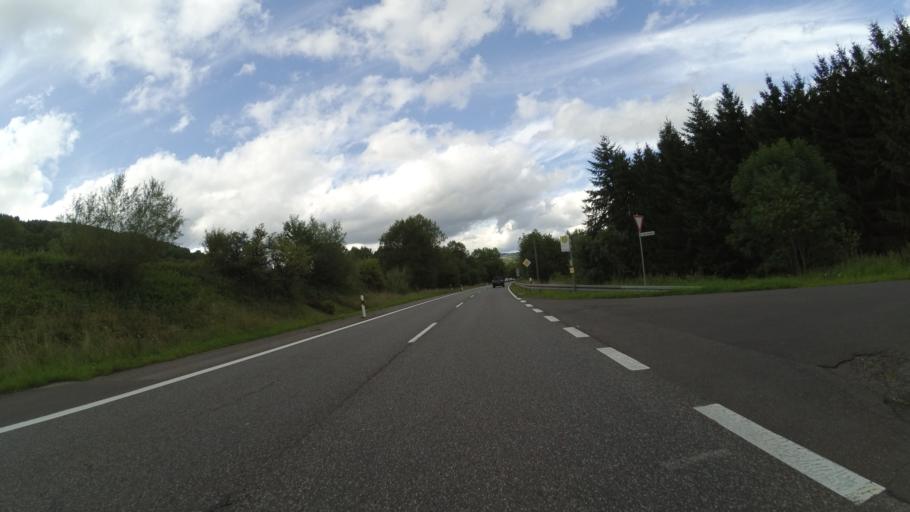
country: DE
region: Saarland
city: Tholey
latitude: 49.5232
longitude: 6.9919
